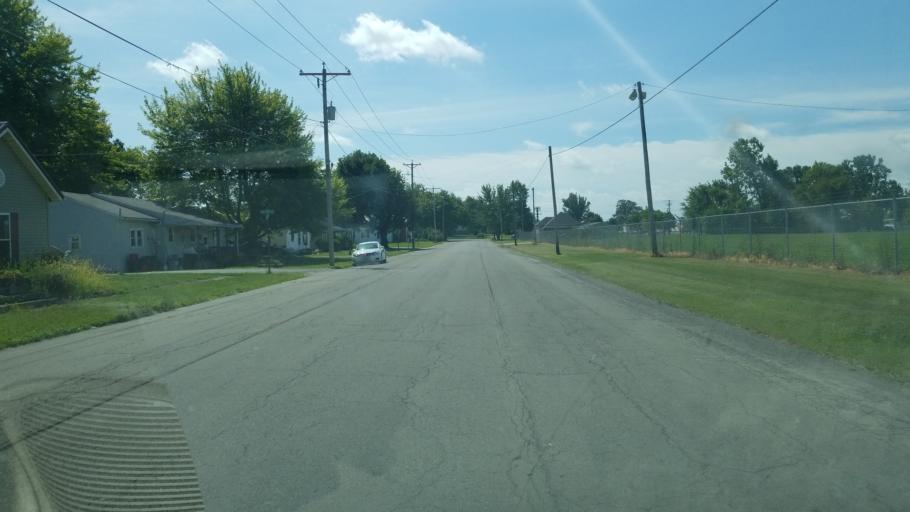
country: US
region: Ohio
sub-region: Hardin County
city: Kenton
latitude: 40.6355
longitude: -83.6082
